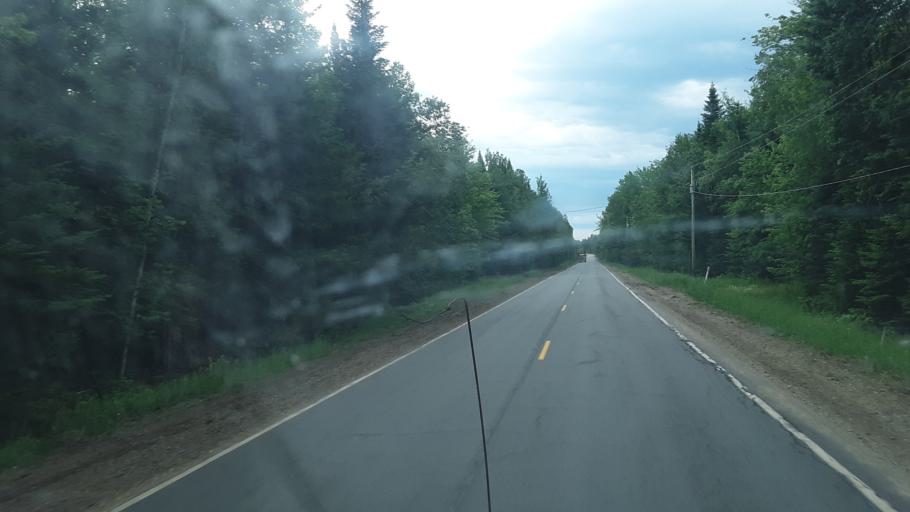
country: US
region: Maine
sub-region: Penobscot County
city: Medway
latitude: 45.6427
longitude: -68.2652
